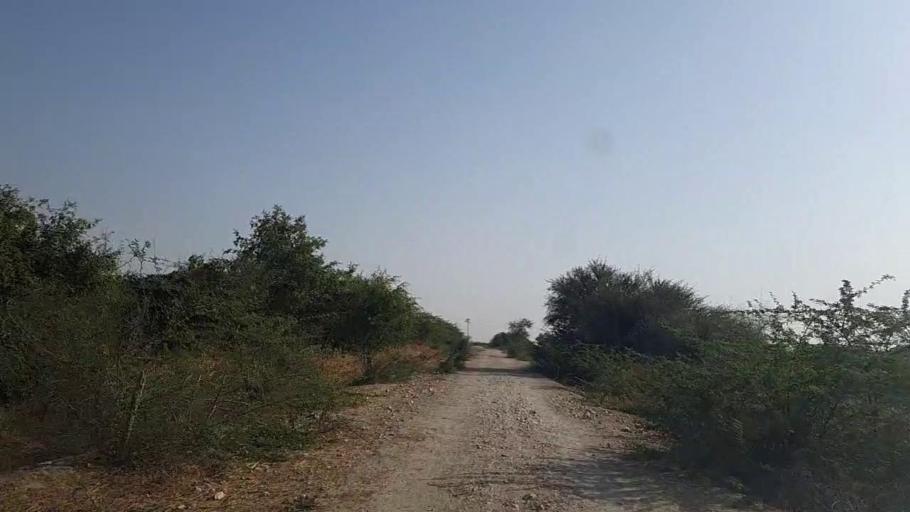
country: PK
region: Sindh
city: Naukot
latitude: 24.6087
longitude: 69.2847
